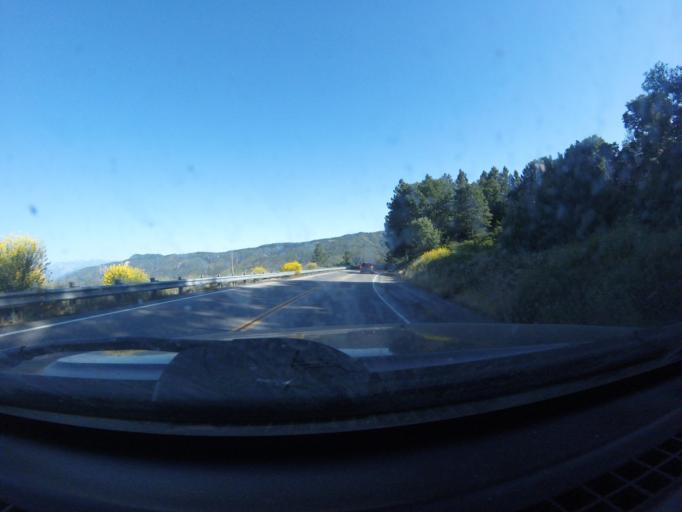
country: US
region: California
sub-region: San Bernardino County
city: Running Springs
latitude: 34.2044
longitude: -117.1495
